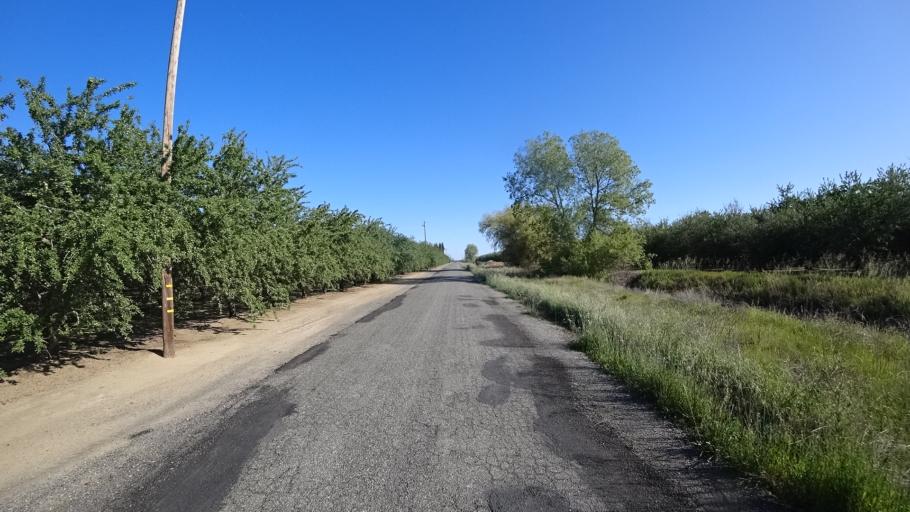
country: US
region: California
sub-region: Glenn County
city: Hamilton City
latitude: 39.6971
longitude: -122.0548
